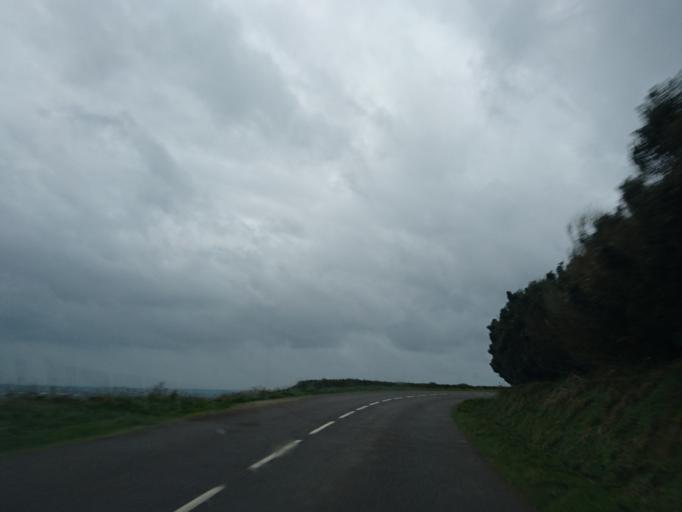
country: FR
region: Brittany
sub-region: Departement du Finistere
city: Le Conquet
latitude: 48.3358
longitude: -4.7728
